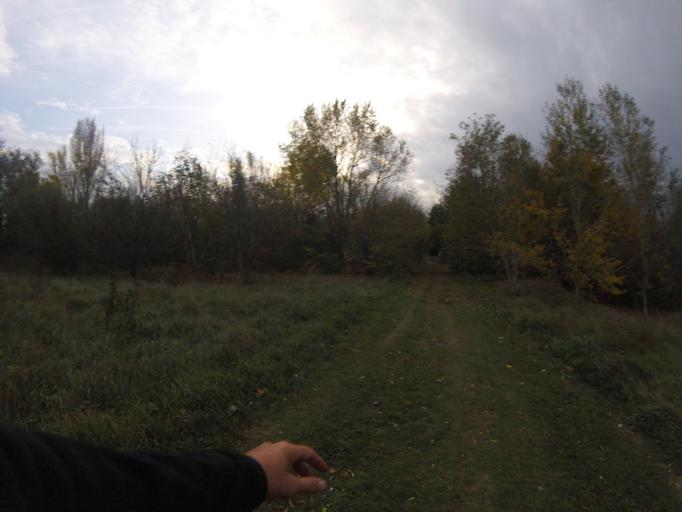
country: HU
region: Fejer
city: Szekesfehervar
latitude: 47.1631
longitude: 18.4148
